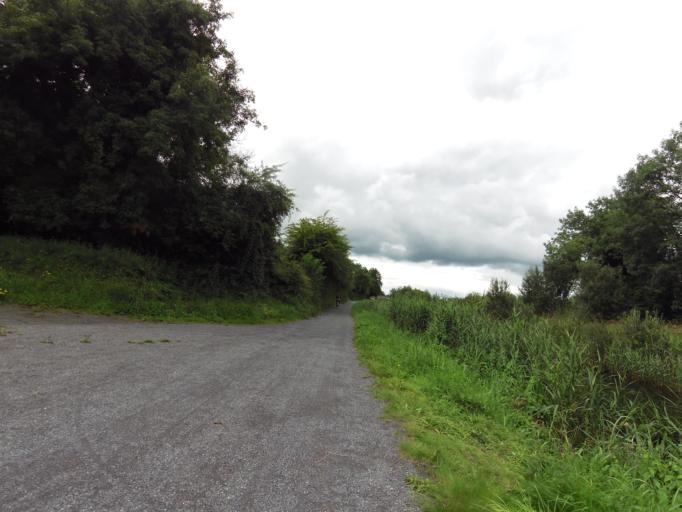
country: IE
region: Leinster
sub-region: An Iarmhi
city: An Muileann gCearr
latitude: 53.5206
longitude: -7.4409
